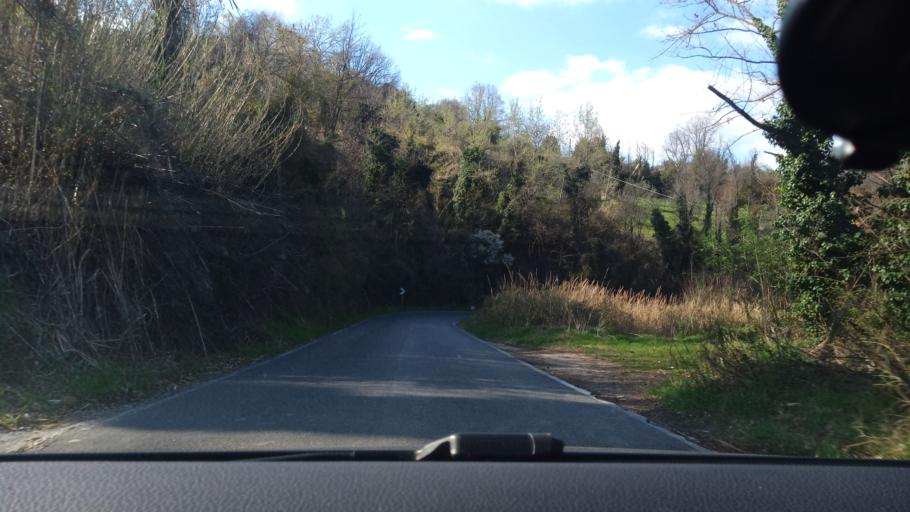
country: IT
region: Latium
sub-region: Citta metropolitana di Roma Capitale
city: Torrita Tiberina
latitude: 42.2478
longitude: 12.6177
